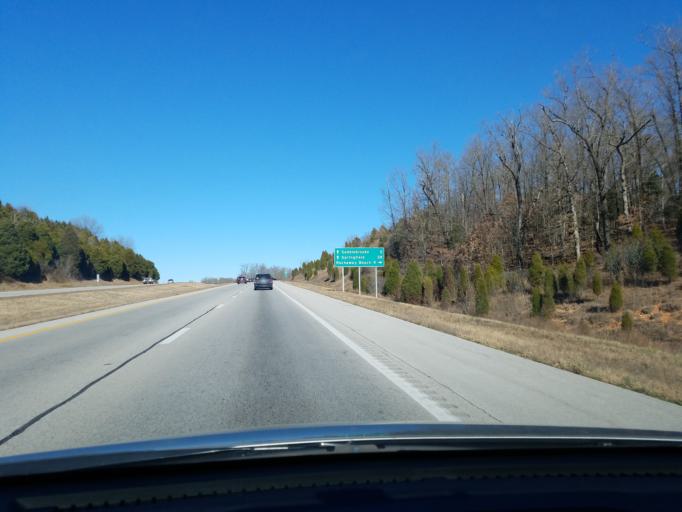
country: US
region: Missouri
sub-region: Taney County
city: Merriam Woods
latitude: 36.7893
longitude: -93.2247
